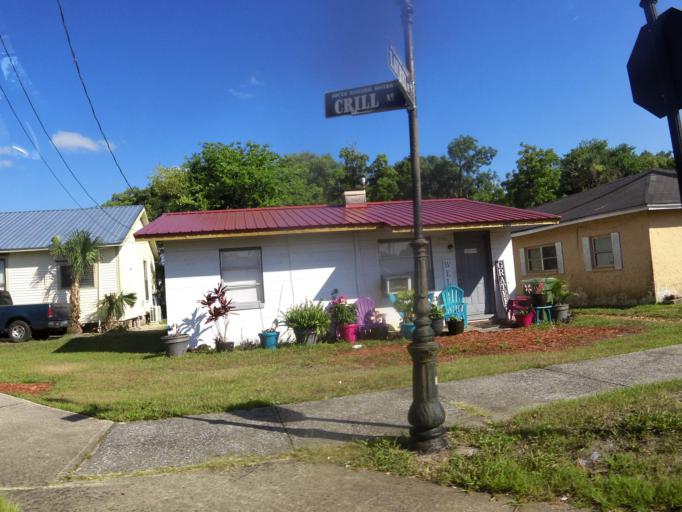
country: US
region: Florida
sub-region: Putnam County
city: Palatka
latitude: 29.6454
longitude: -81.6363
